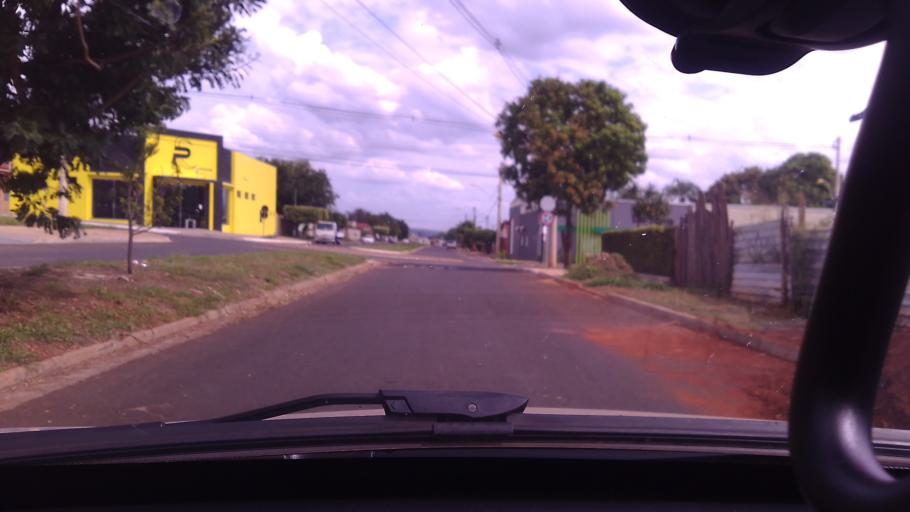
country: BR
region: Goias
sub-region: Mineiros
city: Mineiros
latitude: -17.5783
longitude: -52.5561
